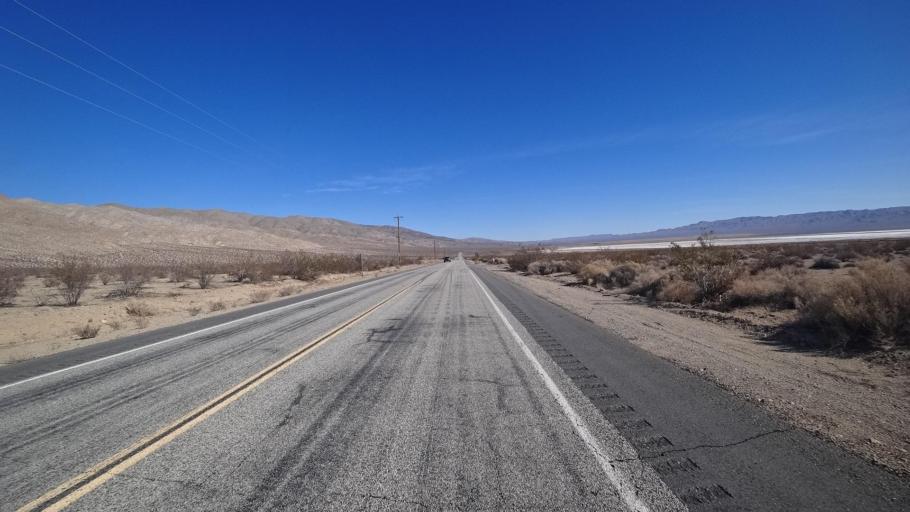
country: US
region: California
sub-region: Kern County
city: California City
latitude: 35.3637
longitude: -117.8945
